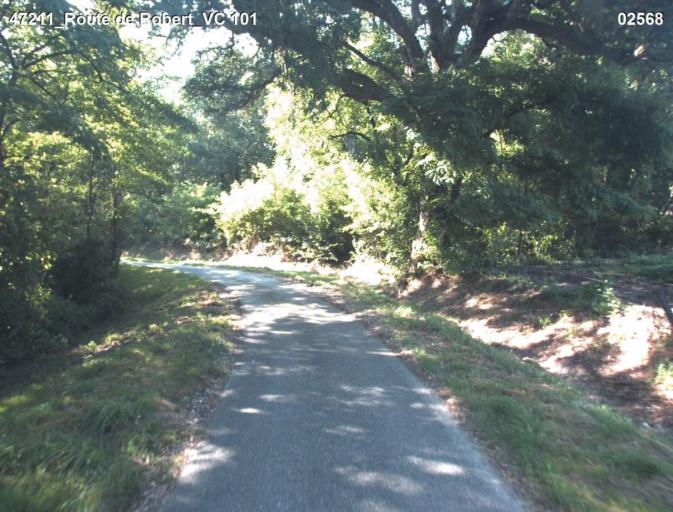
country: FR
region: Aquitaine
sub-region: Departement du Lot-et-Garonne
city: Mezin
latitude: 44.0532
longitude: 0.1806
